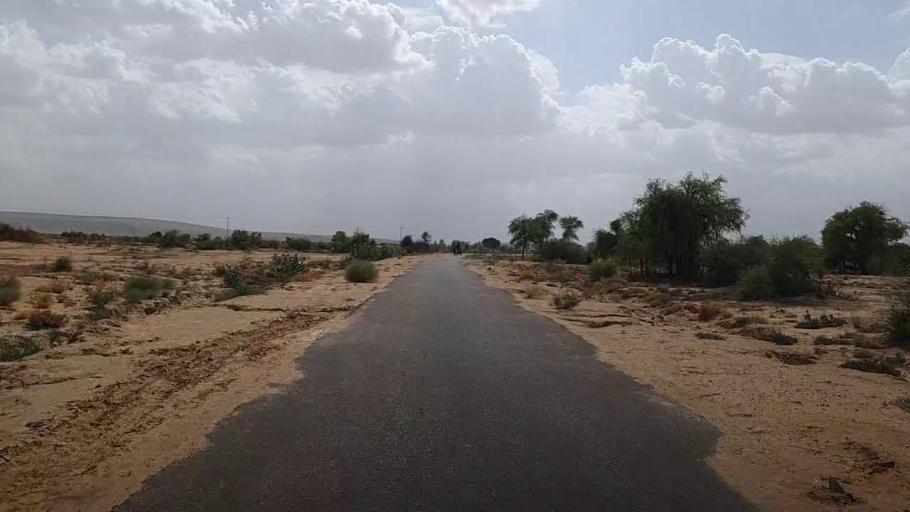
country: PK
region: Sindh
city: Jamshoro
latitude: 25.4035
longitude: 67.7833
